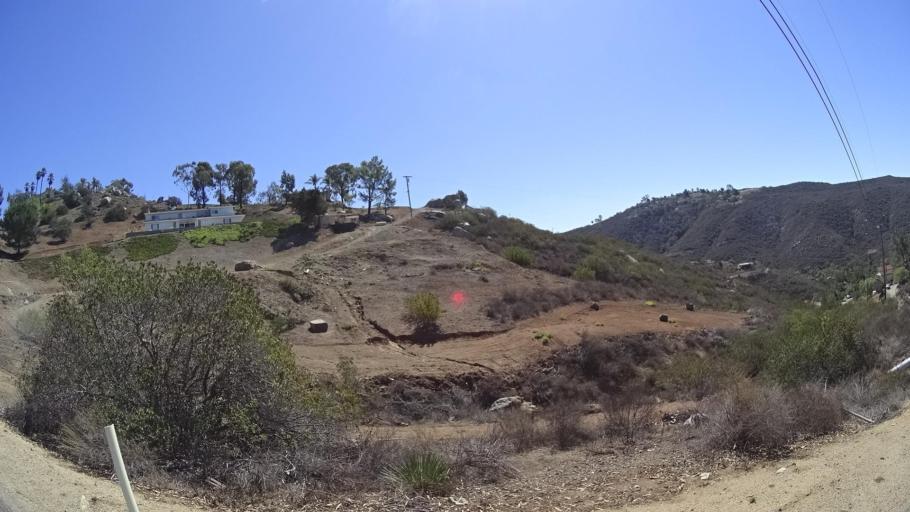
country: US
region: California
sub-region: San Diego County
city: Jamul
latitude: 32.7385
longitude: -116.8807
